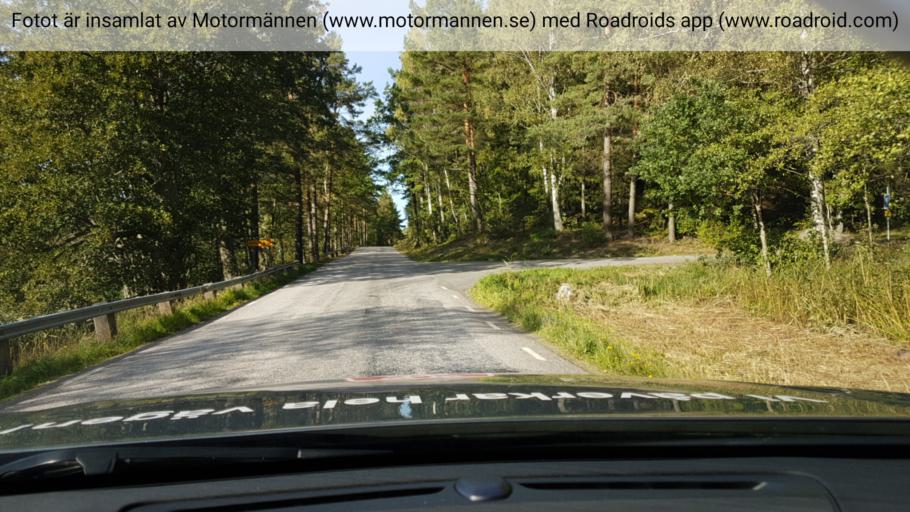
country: SE
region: OEstergoetland
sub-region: Valdemarsviks Kommun
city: Valdemarsvik
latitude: 58.1433
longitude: 16.6155
